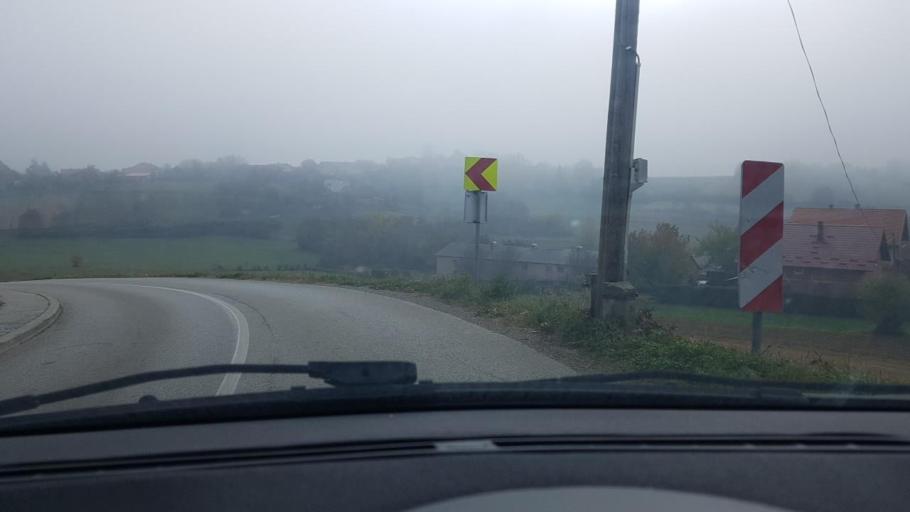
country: HR
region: Krapinsko-Zagorska
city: Zlatar
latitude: 46.1500
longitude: 16.0484
